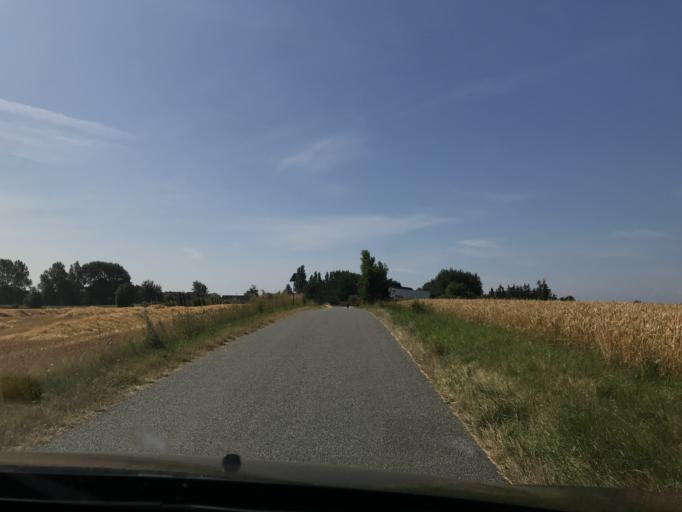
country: DK
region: South Denmark
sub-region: AEro Kommune
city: AEroskobing
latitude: 54.9350
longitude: 10.2825
